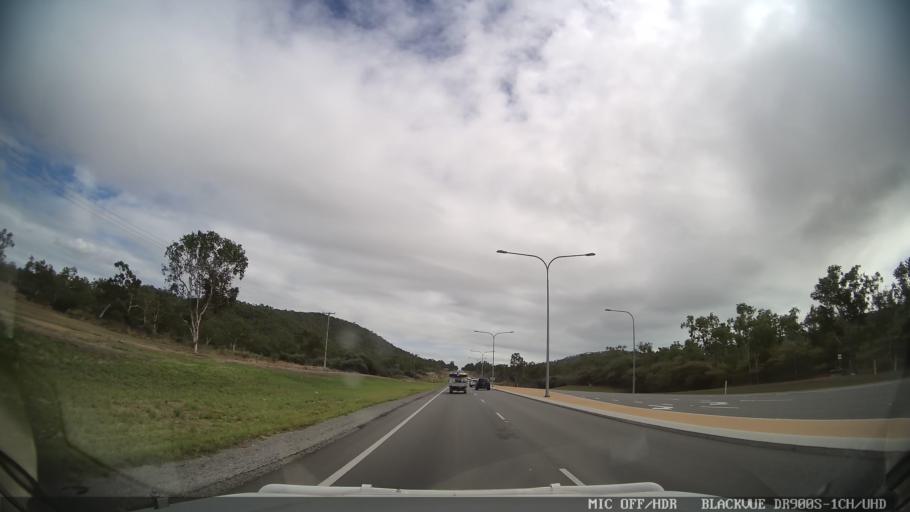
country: AU
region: Queensland
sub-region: Townsville
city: Townsville
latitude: -19.3707
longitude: 146.8972
